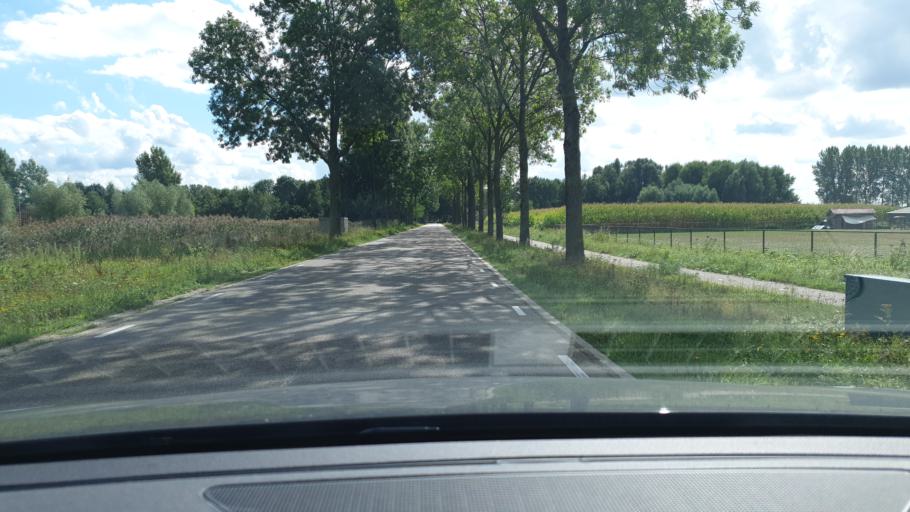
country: NL
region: North Brabant
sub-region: Gemeente Veghel
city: Zijtaart
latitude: 51.5960
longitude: 5.5262
